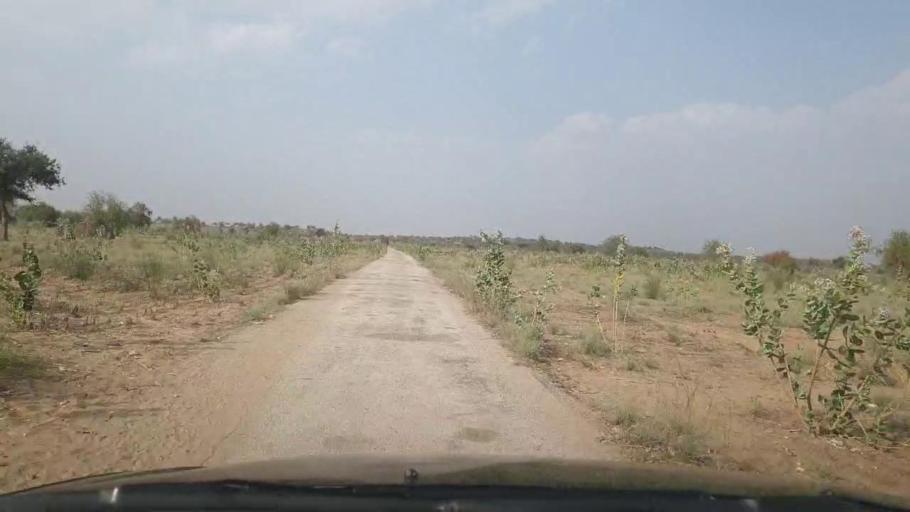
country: PK
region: Sindh
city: Islamkot
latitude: 25.0350
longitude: 70.5614
